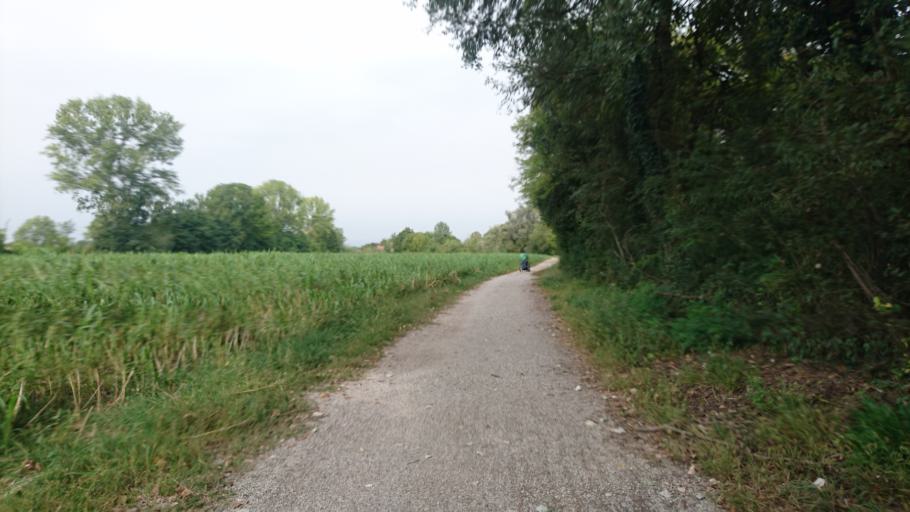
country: IT
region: Veneto
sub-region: Provincia di Padova
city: Grantorto
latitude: 45.5742
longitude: 11.7586
